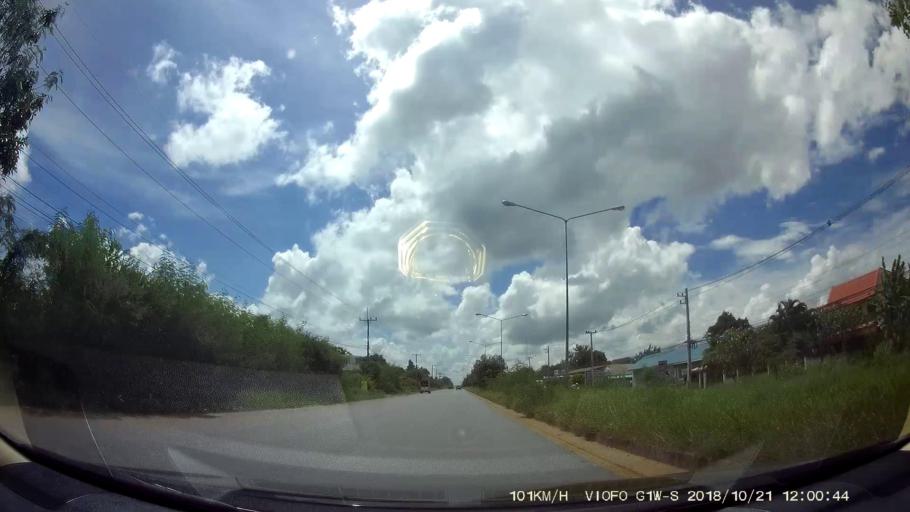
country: TH
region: Chaiyaphum
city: Chatturat
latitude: 15.5472
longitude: 101.8405
